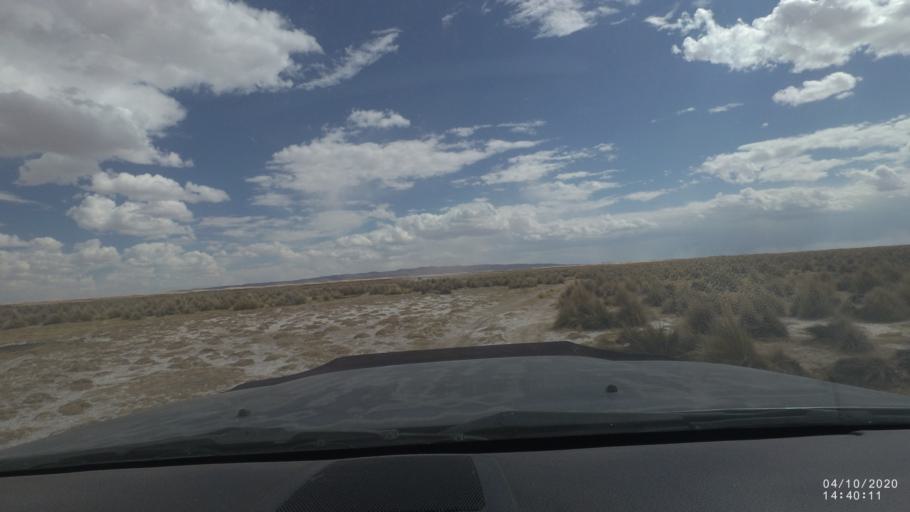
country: BO
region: Oruro
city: Poopo
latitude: -18.6786
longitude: -67.4896
